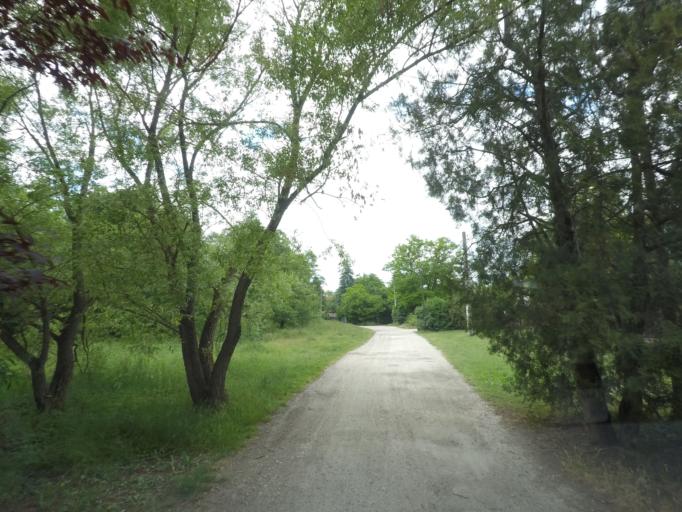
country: HU
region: Pest
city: Szentendre
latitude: 47.6783
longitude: 19.0554
